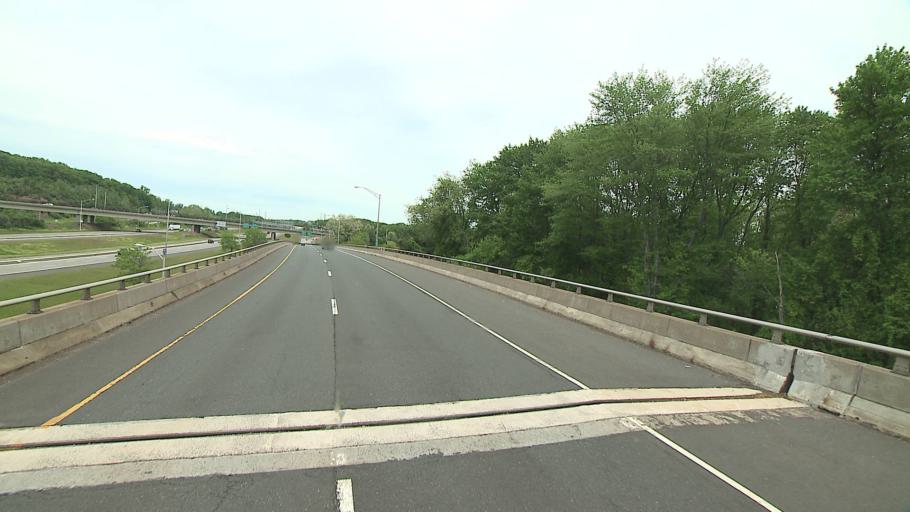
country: US
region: Connecticut
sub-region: Hartford County
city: East Hartford
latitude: 41.7774
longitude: -72.5714
